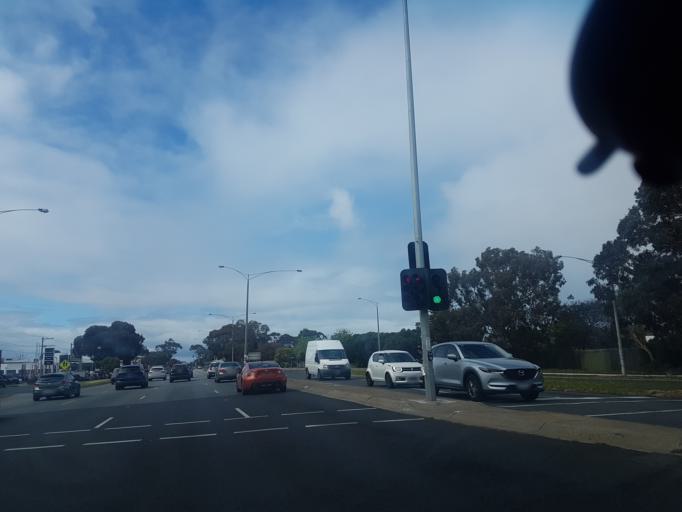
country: AU
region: Victoria
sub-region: Glen Eira
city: Bentleigh
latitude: -37.9206
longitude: 145.0223
